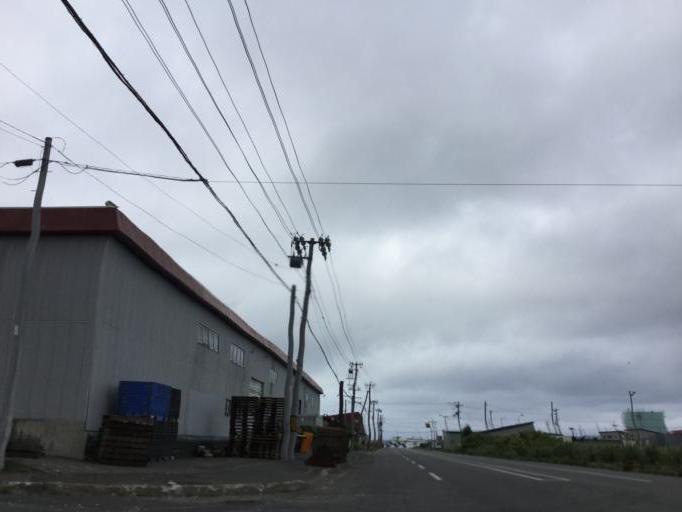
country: JP
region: Hokkaido
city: Wakkanai
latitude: 45.4064
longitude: 141.6822
